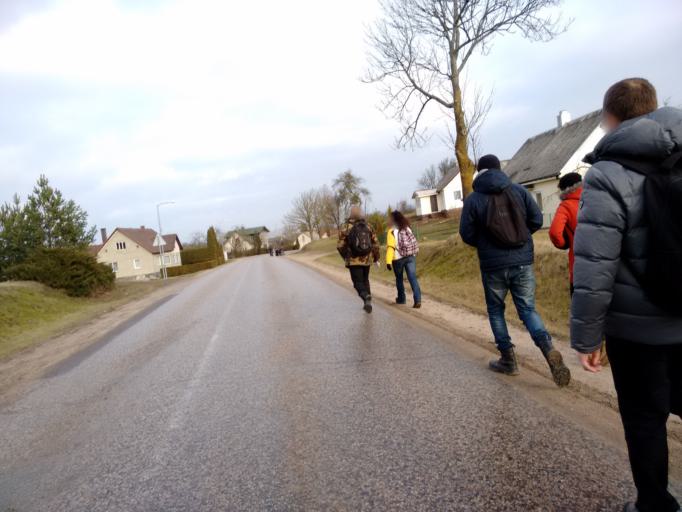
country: LT
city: Veisiejai
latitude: 54.2316
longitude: 23.8199
